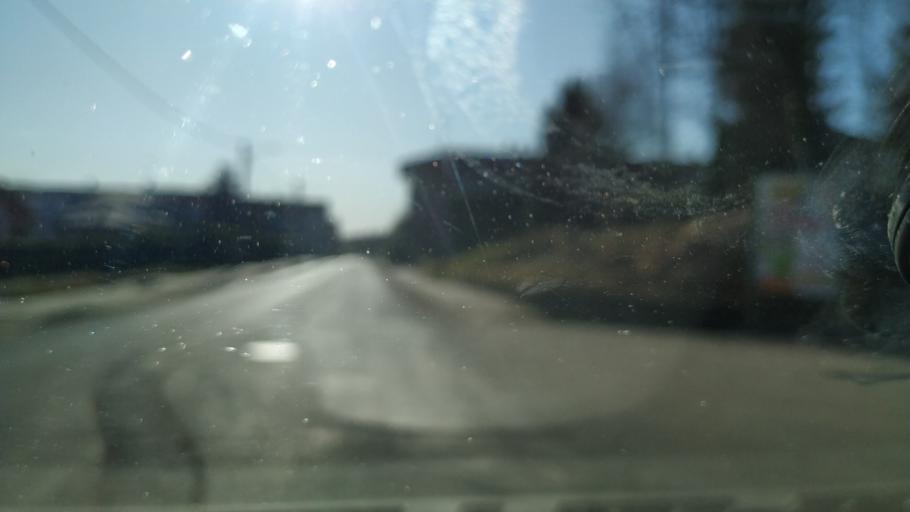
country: IT
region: Piedmont
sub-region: Provincia di Vercelli
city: Lozzolo
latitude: 45.6220
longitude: 8.3224
